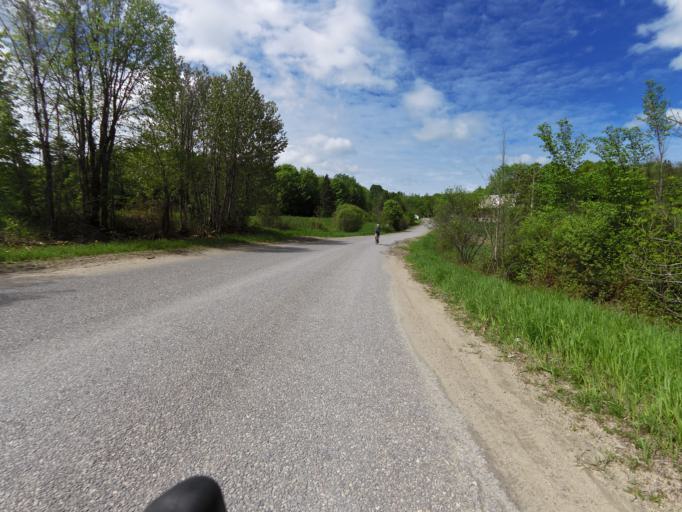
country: CA
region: Quebec
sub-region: Outaouais
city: Wakefield
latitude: 45.7839
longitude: -76.0140
